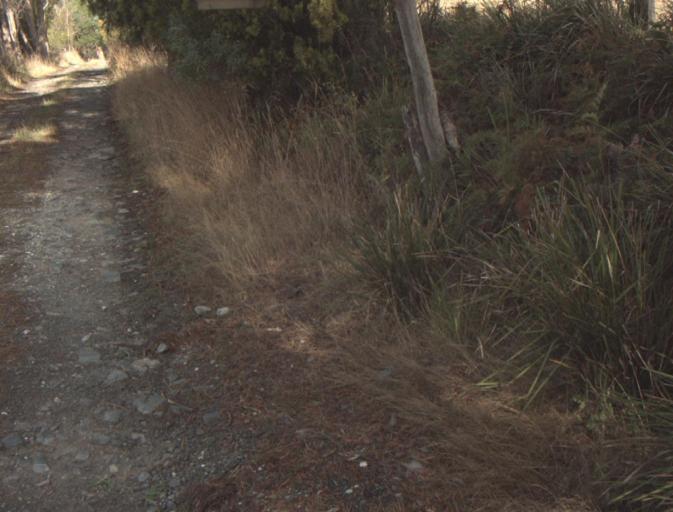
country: AU
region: Tasmania
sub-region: Launceston
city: Mayfield
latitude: -41.2208
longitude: 147.1573
